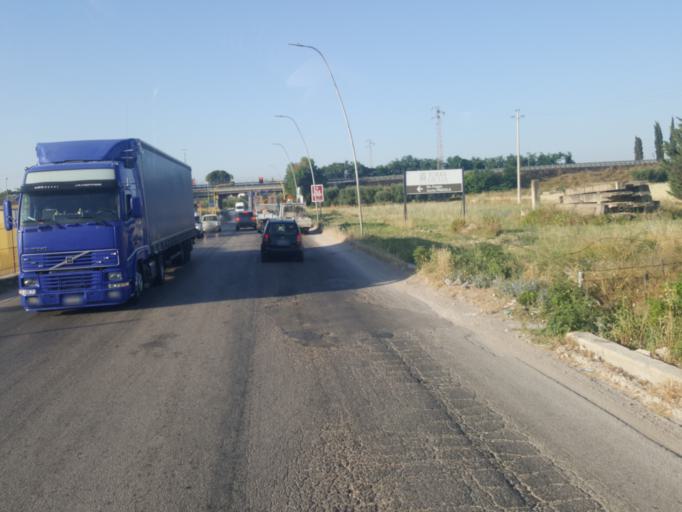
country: IT
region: Apulia
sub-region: Provincia di Foggia
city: Cerignola
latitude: 41.2828
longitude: 15.8959
